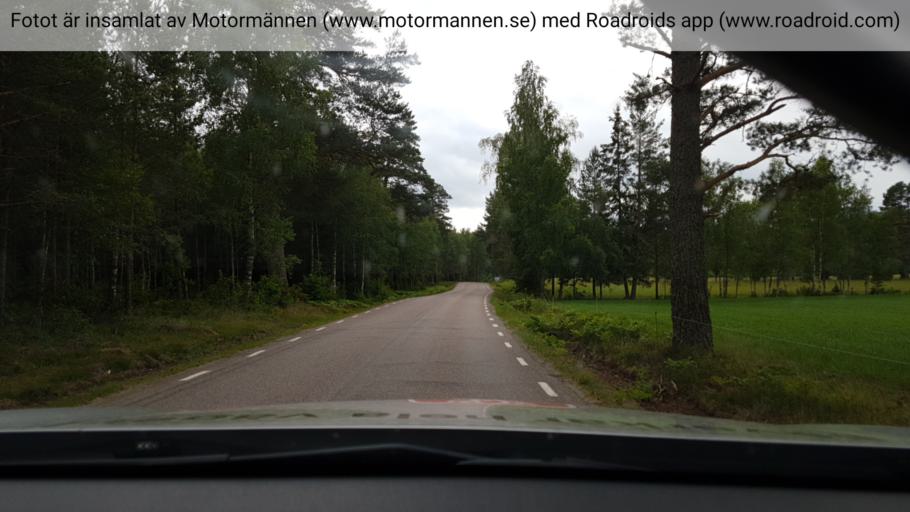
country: SE
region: Joenkoeping
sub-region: Habo Kommun
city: Habo
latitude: 58.0315
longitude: 14.0183
